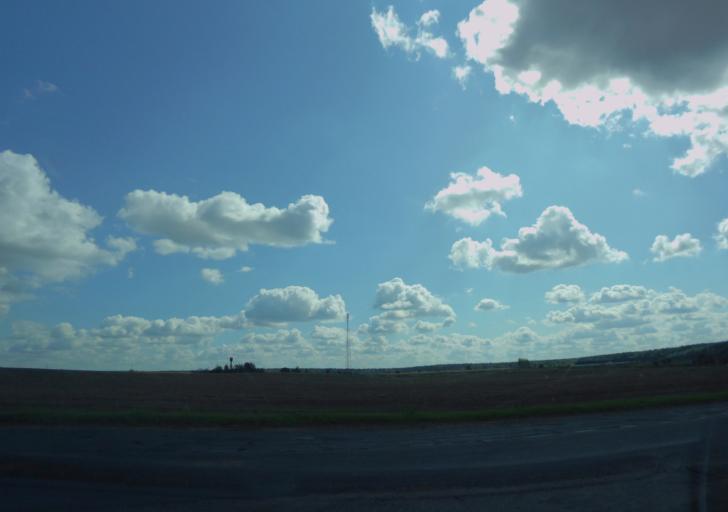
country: BY
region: Minsk
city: Zyembin
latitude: 54.4058
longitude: 28.4019
